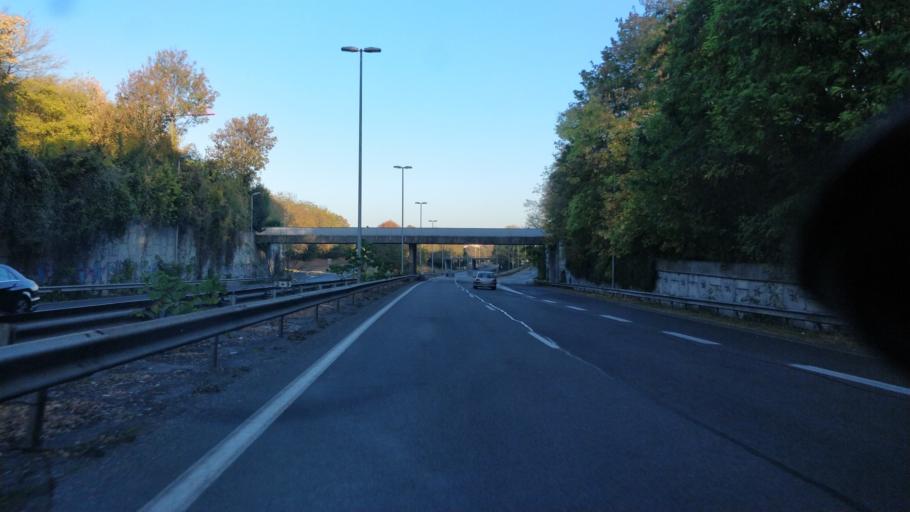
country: FR
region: Ile-de-France
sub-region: Departement de Seine-et-Marne
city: Noisiel
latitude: 48.8488
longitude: 2.6162
